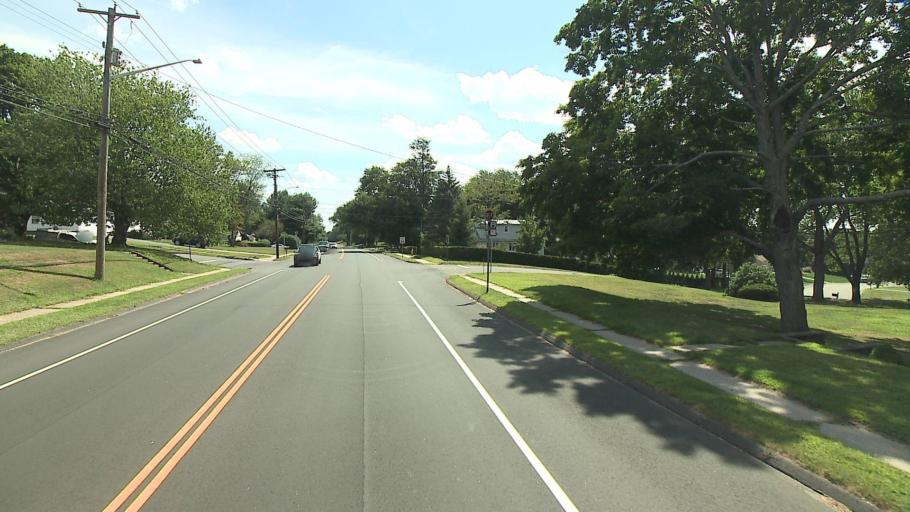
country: US
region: Connecticut
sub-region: Fairfield County
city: Stratford
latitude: 41.2271
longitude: -73.1526
